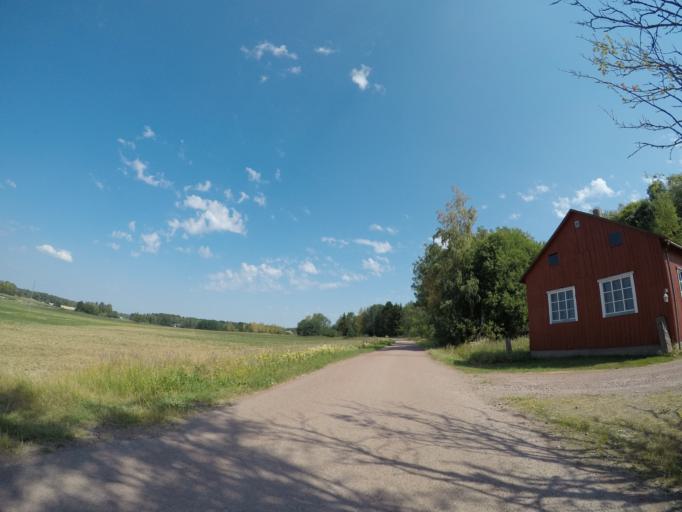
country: AX
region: Alands landsbygd
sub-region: Finstroem
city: Finstroem
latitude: 60.2081
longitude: 19.9026
